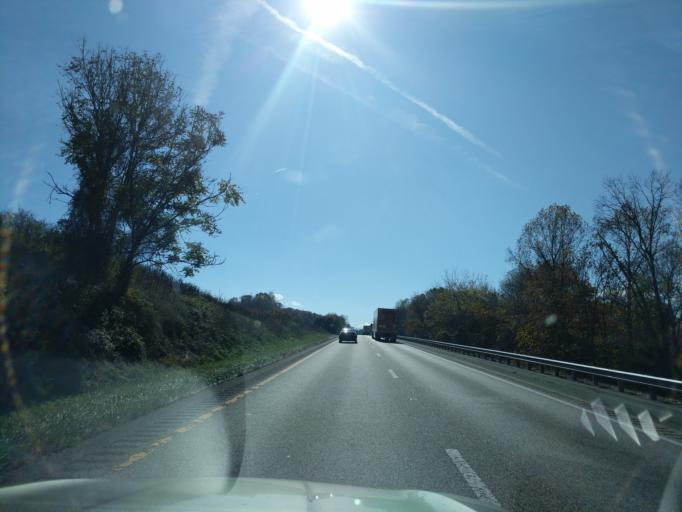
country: US
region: Virginia
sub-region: Rockbridge County
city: East Lexington
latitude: 37.7658
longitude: -79.4057
